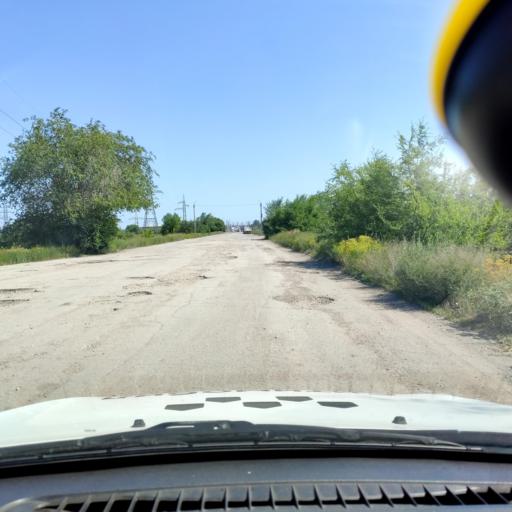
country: RU
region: Samara
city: Zhigulevsk
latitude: 53.5392
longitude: 49.5108
